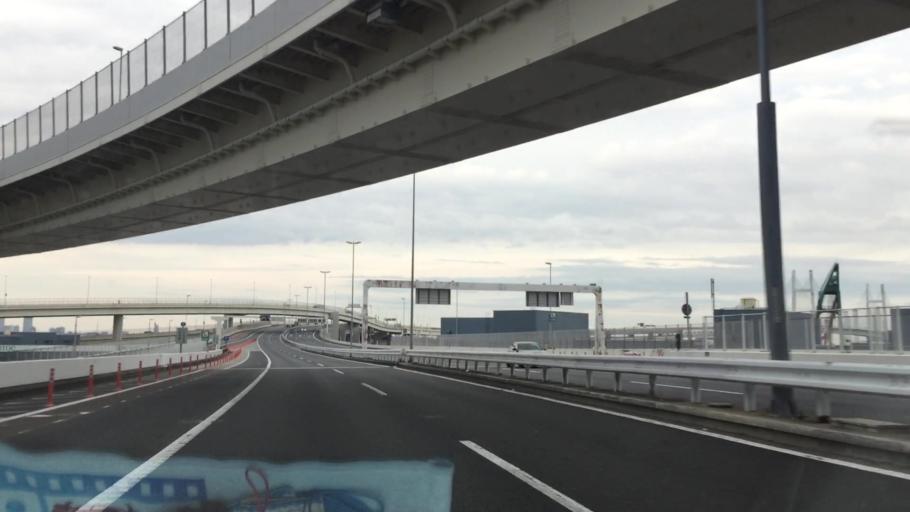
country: JP
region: Kanagawa
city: Yokohama
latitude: 35.4363
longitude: 139.6690
